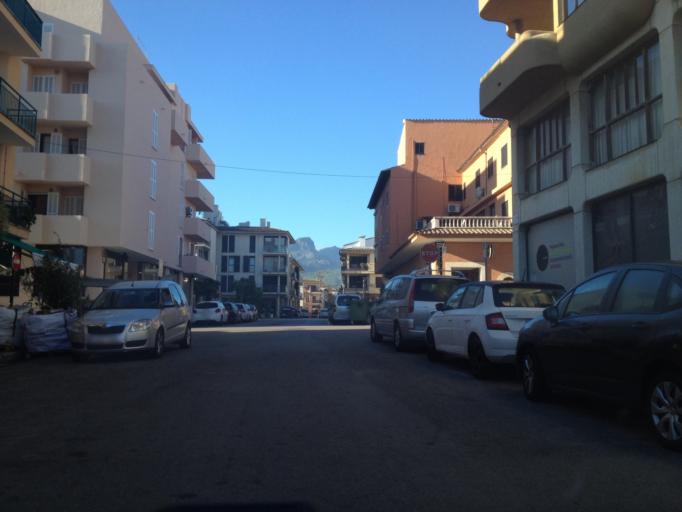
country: ES
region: Balearic Islands
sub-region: Illes Balears
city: Pollenca
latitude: 39.8772
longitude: 3.0200
